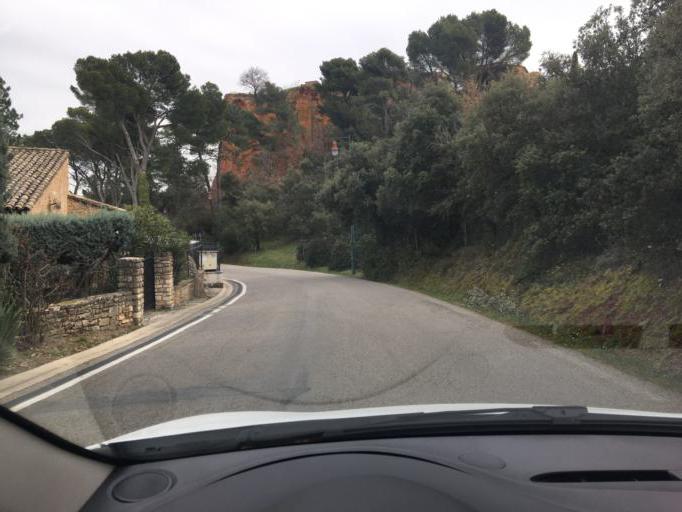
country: FR
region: Provence-Alpes-Cote d'Azur
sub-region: Departement du Vaucluse
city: Roussillon
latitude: 43.9037
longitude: 5.2903
